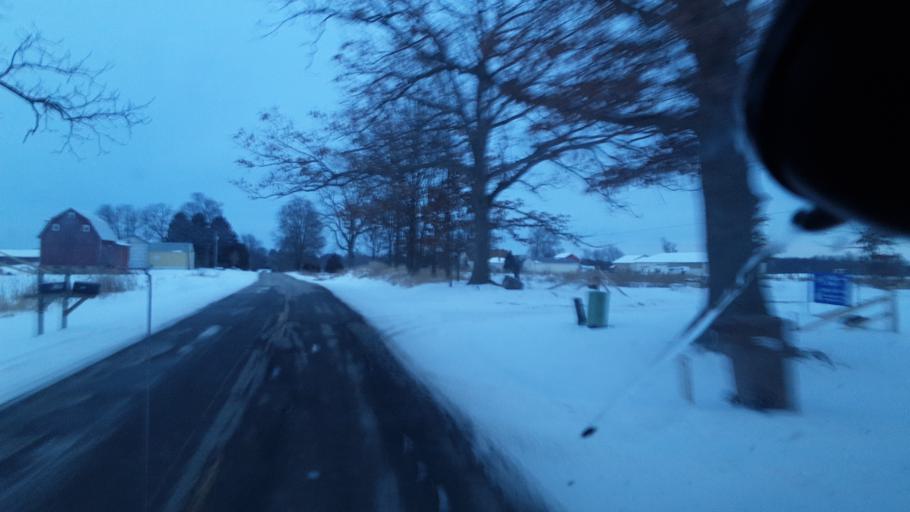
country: US
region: Michigan
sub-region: Ingham County
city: Stockbridge
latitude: 42.4082
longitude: -84.2902
